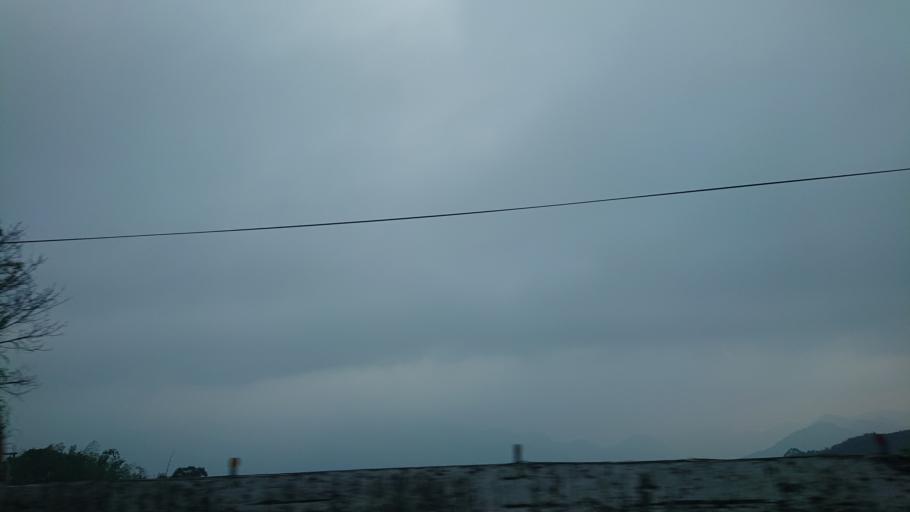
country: TW
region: Taiwan
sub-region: Chiayi
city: Jiayi Shi
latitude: 23.4724
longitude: 120.7026
